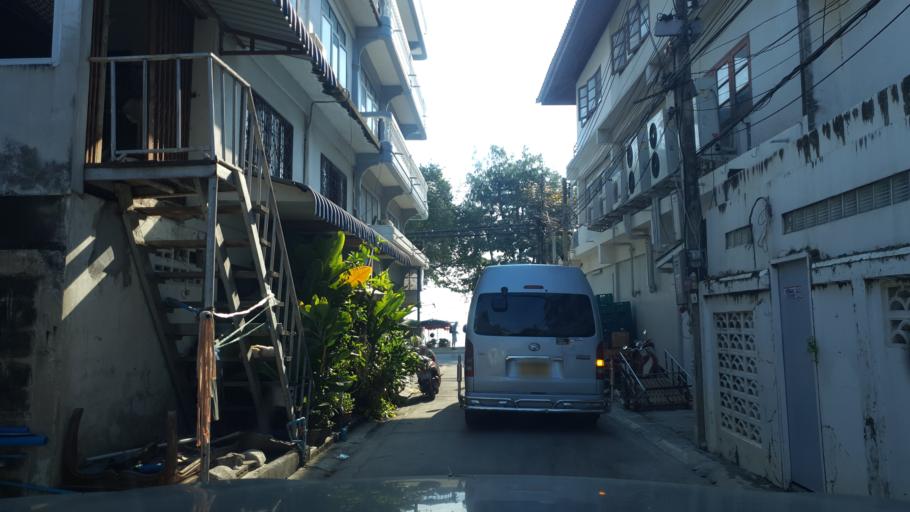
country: TH
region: Phetchaburi
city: Cha-am
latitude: 12.7973
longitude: 99.9844
